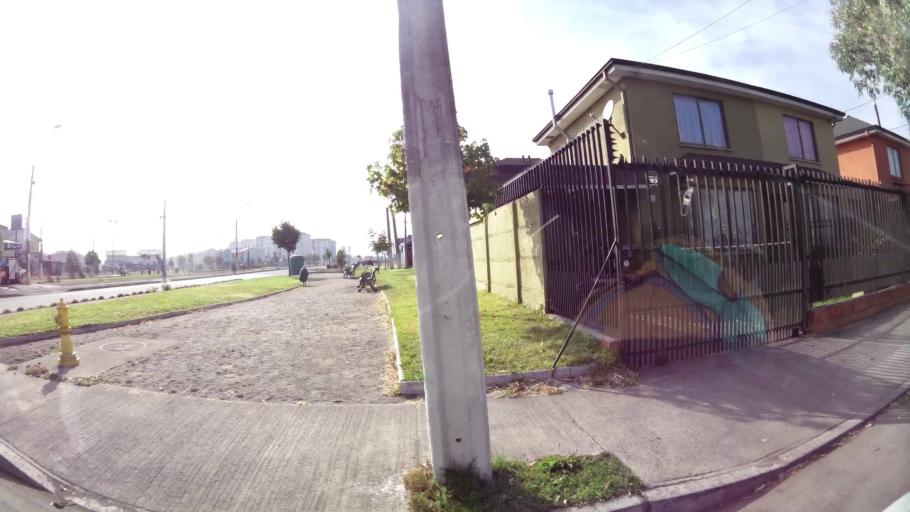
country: CL
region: Biobio
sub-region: Provincia de Concepcion
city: Concepcion
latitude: -36.7988
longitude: -73.1119
